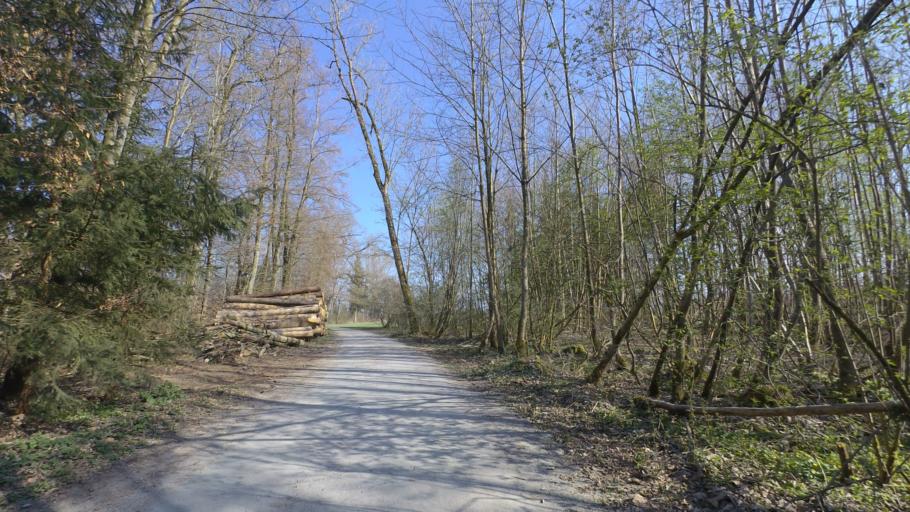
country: DE
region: Bavaria
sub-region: Upper Bavaria
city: Traunreut
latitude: 47.9504
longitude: 12.5892
